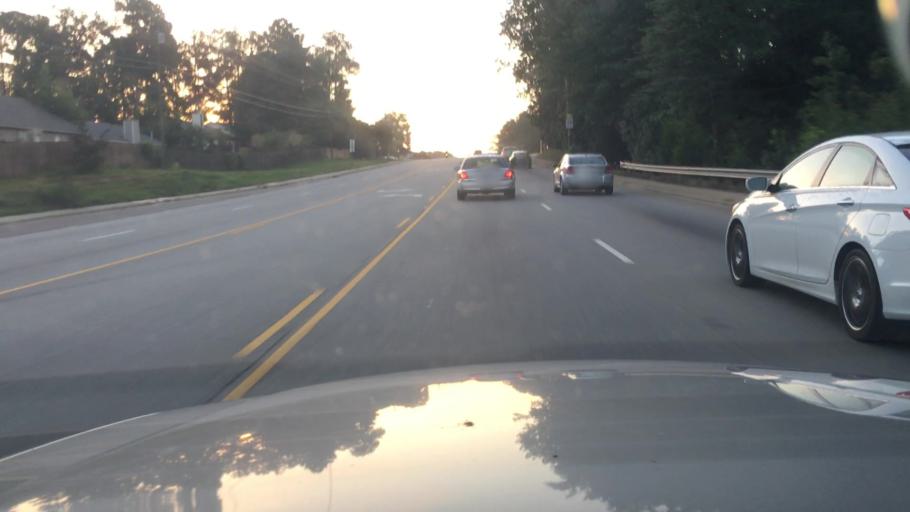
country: US
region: North Carolina
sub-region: Cumberland County
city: Fort Bragg
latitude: 35.0579
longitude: -78.9981
